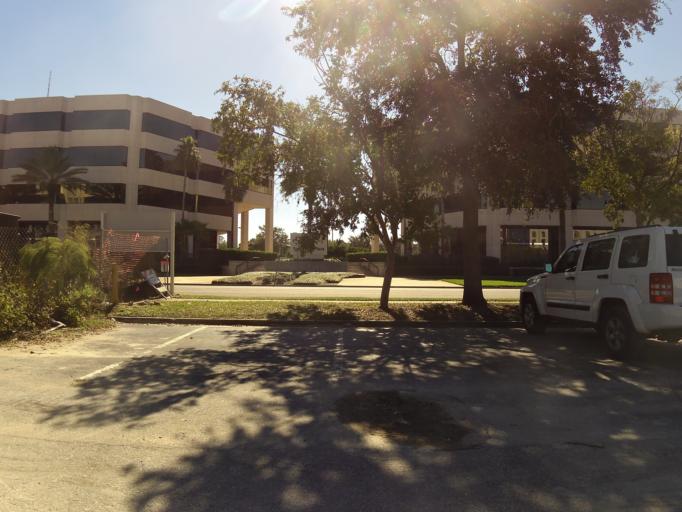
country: US
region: Florida
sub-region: Duval County
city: Jacksonville
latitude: 30.3165
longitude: -81.6521
